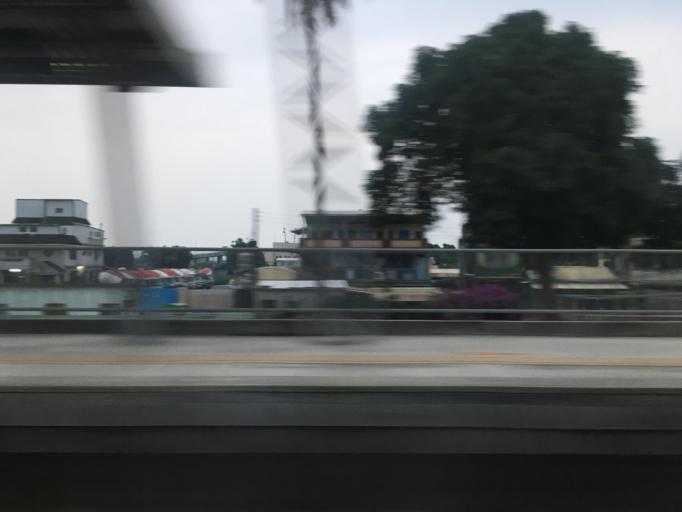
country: TW
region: Taiwan
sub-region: Pingtung
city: Pingtung
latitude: 22.6657
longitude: 120.4648
